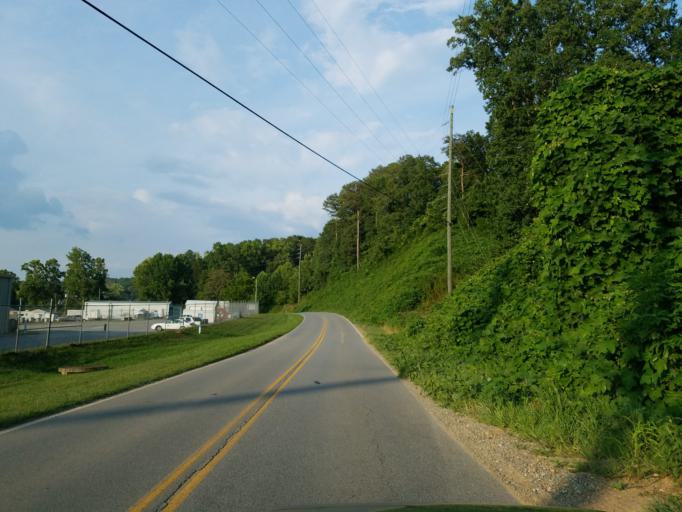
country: US
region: Georgia
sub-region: Gilmer County
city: Ellijay
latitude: 34.6674
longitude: -84.4947
